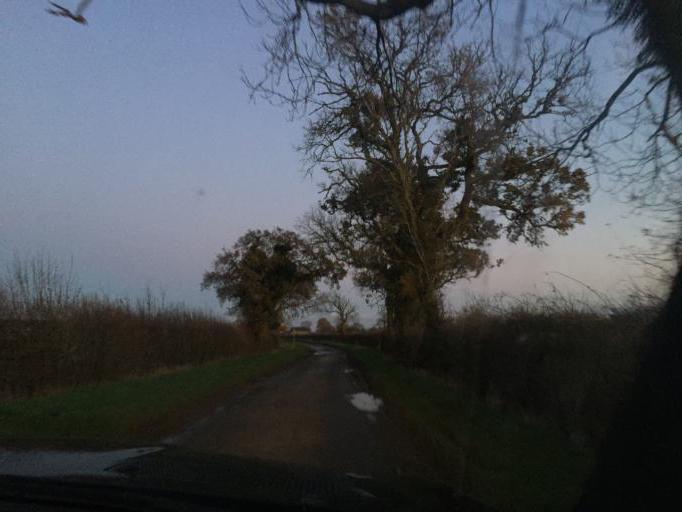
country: GB
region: England
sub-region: Northamptonshire
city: Brackley
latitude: 52.0894
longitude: -1.1016
